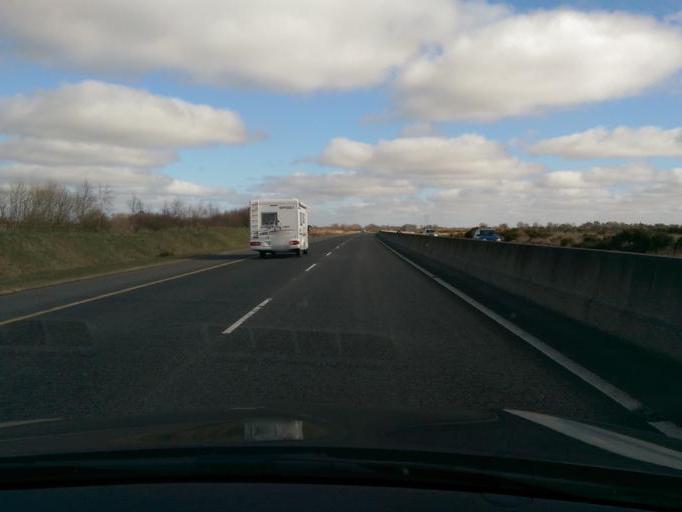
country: IE
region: Leinster
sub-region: An Iarmhi
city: Rochfortbridge
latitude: 53.4402
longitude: -7.2087
